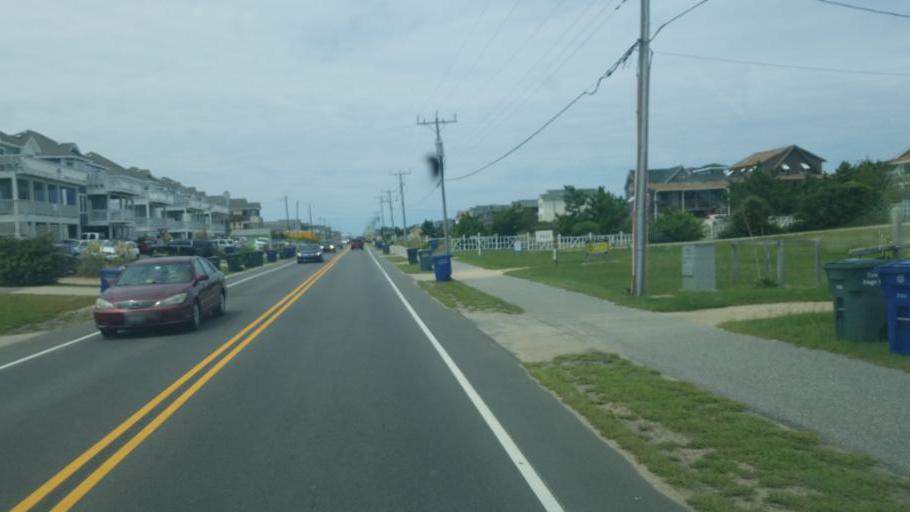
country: US
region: North Carolina
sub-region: Dare County
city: Nags Head
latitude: 35.9662
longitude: -75.6291
